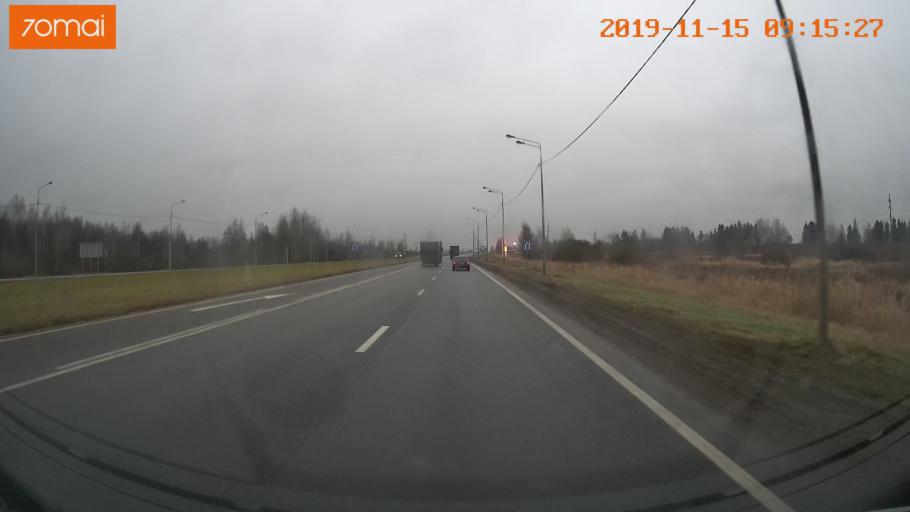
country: RU
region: Vologda
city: Tonshalovo
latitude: 59.2388
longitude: 37.9669
